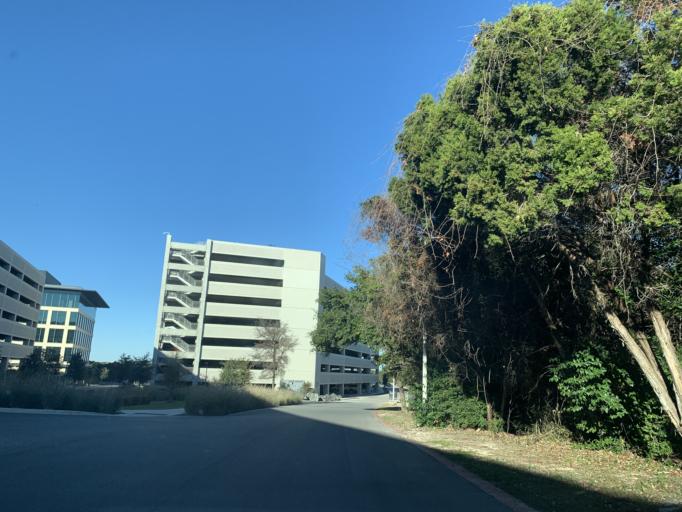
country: US
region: Texas
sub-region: Travis County
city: Wells Branch
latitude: 30.3982
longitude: -97.7111
